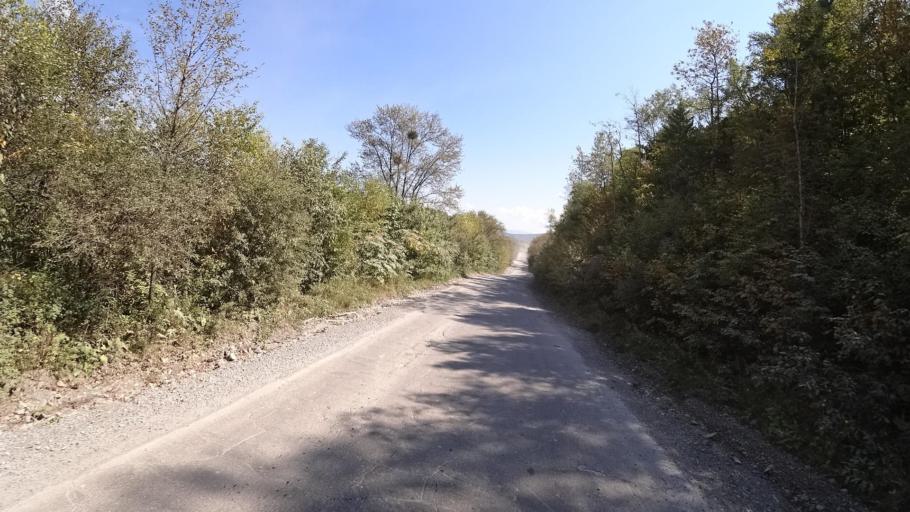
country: RU
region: Jewish Autonomous Oblast
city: Londoko
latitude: 49.0072
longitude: 131.9084
